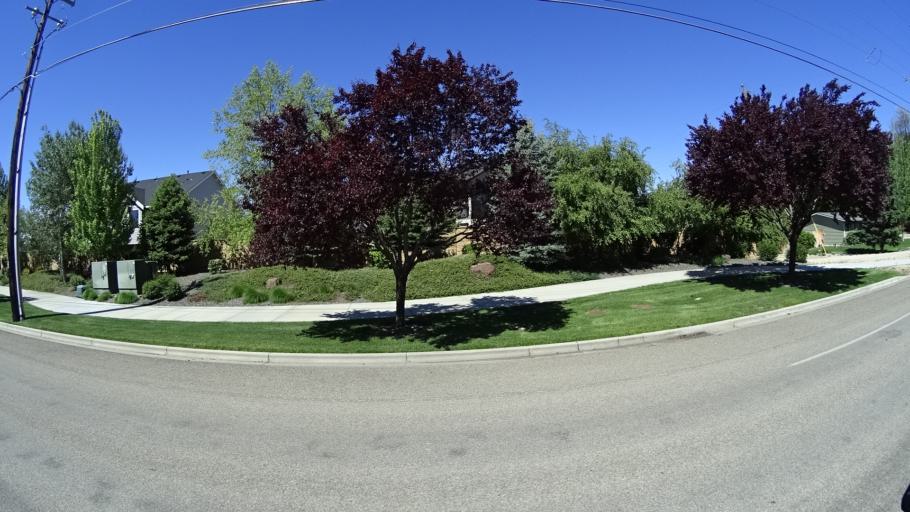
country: US
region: Idaho
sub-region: Ada County
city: Eagle
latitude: 43.6573
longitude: -116.3745
